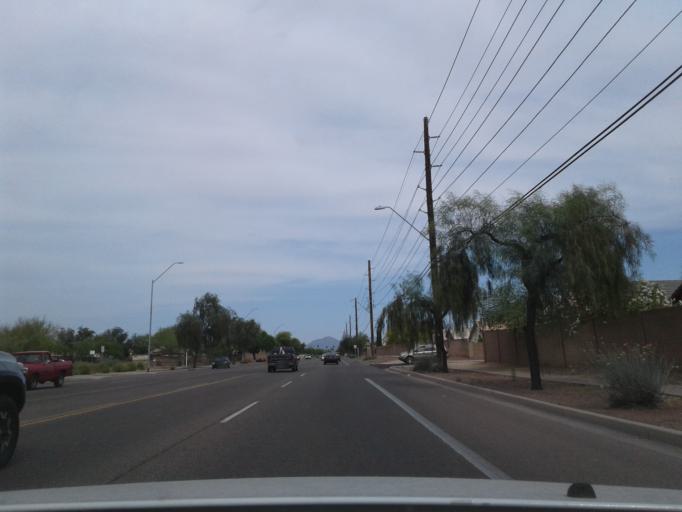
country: US
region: Arizona
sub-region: Maricopa County
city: Glendale
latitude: 33.6546
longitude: -112.0782
